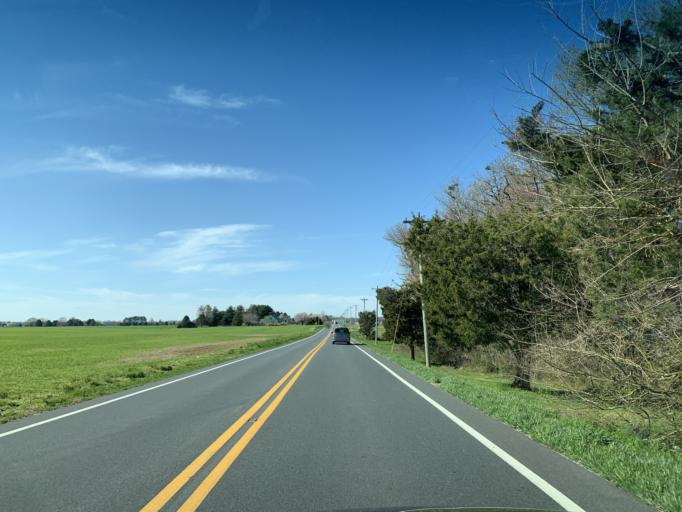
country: US
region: Delaware
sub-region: Kent County
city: Riverview
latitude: 38.9701
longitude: -75.4953
